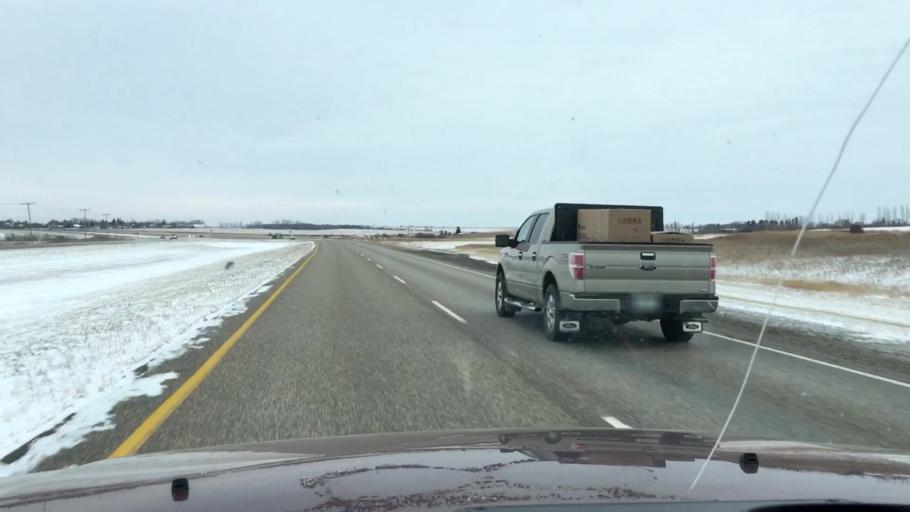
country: CA
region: Saskatchewan
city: Moose Jaw
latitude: 50.9517
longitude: -105.7081
